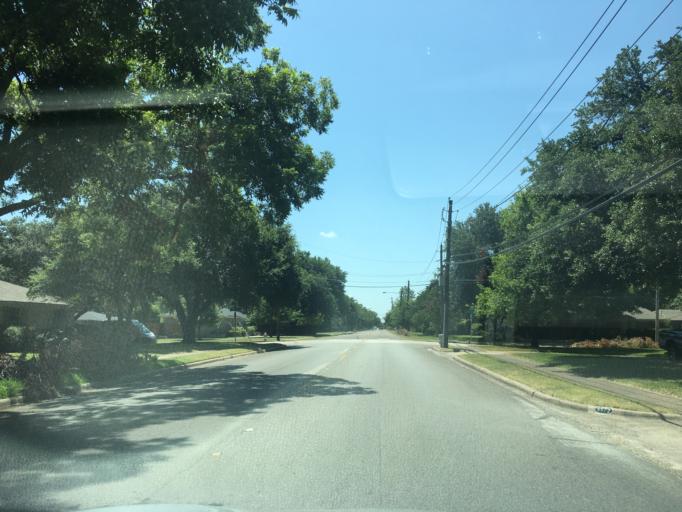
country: US
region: Texas
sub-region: Dallas County
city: Highland Park
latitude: 32.8507
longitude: -96.7467
